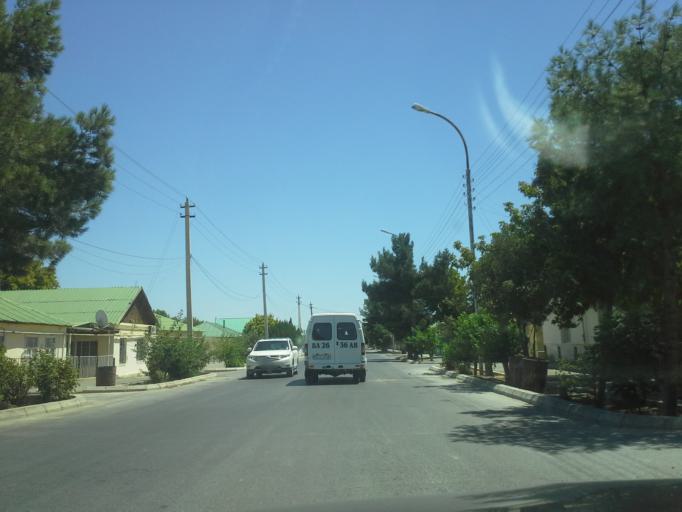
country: TM
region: Ahal
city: Abadan
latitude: 38.0212
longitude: 58.2547
